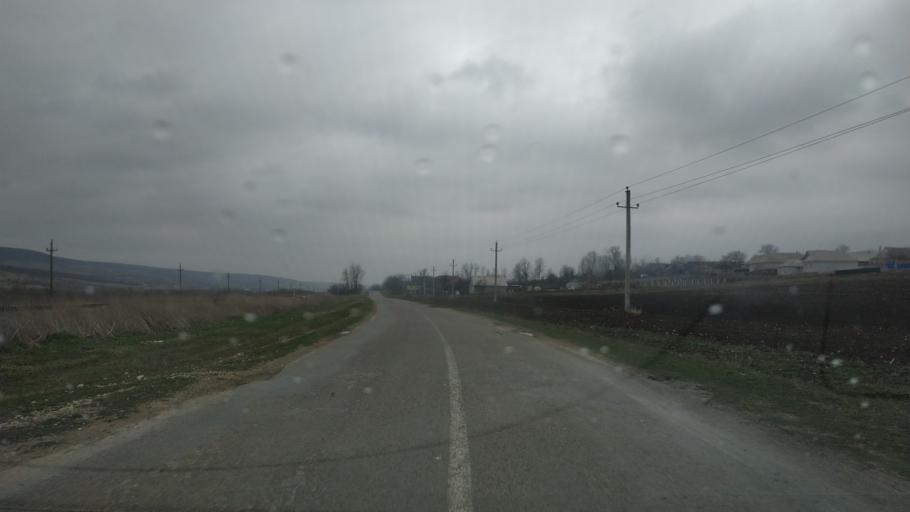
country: MD
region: Cantemir
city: Cantemir
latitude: 46.3287
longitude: 28.2863
